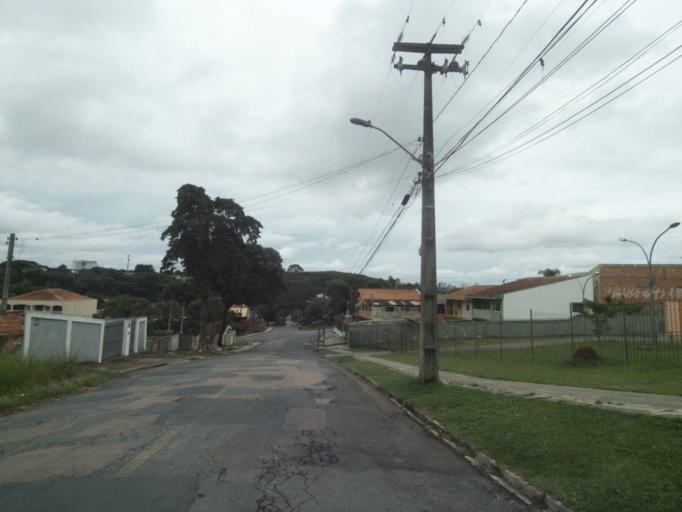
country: BR
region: Parana
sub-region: Curitiba
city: Curitiba
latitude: -25.4569
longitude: -49.3253
